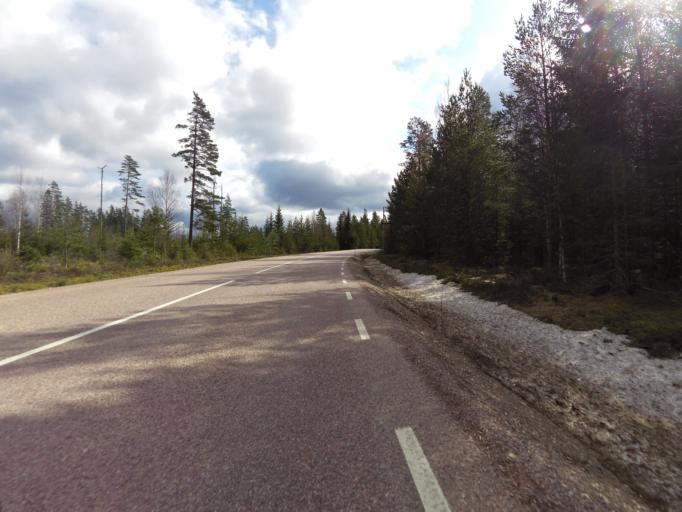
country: SE
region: Dalarna
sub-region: Avesta Kommun
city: Horndal
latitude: 60.3024
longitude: 16.2669
